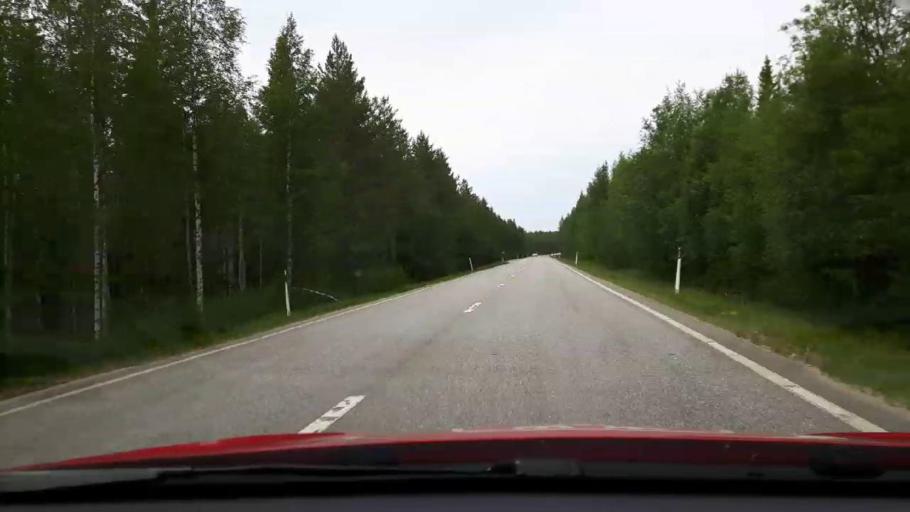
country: SE
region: Jaemtland
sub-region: Harjedalens Kommun
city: Sveg
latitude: 62.1072
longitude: 14.1971
